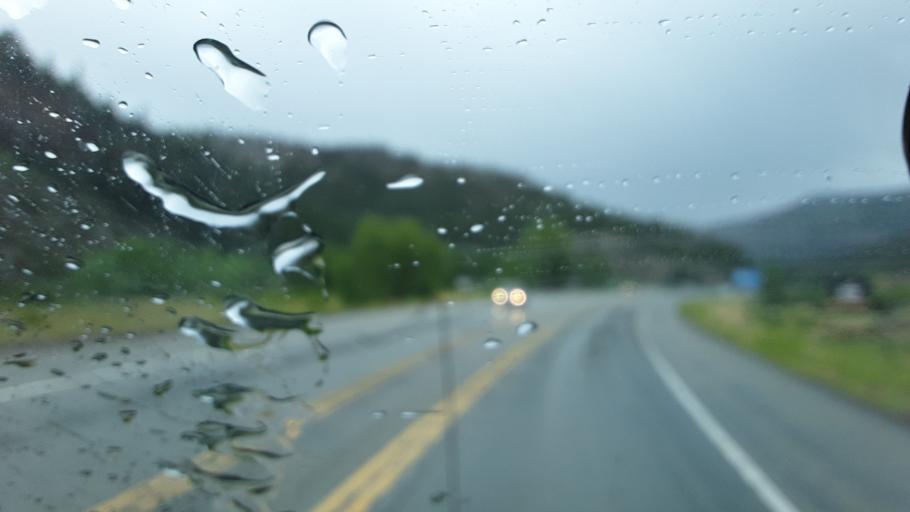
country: US
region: Colorado
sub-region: Mineral County
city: Creede
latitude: 37.6089
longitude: -106.7186
